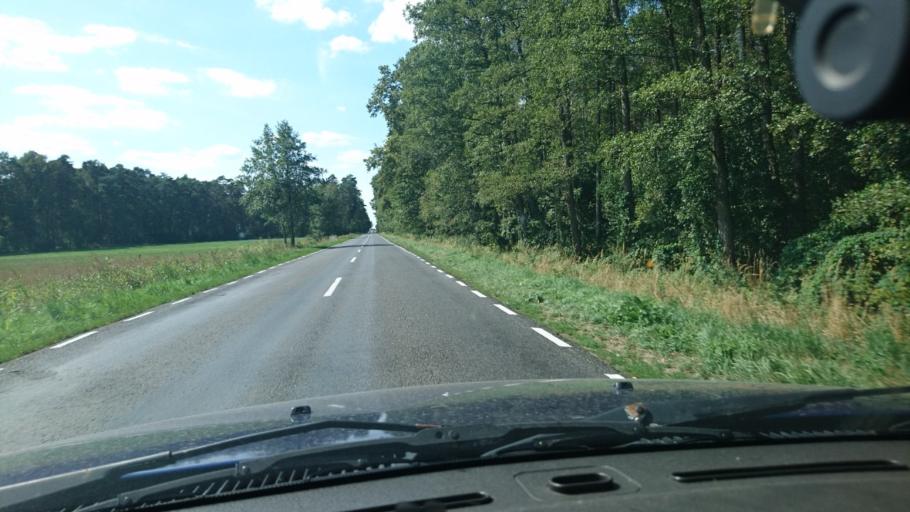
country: PL
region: Greater Poland Voivodeship
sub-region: Powiat krotoszynski
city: Sulmierzyce
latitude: 51.6024
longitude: 17.5829
